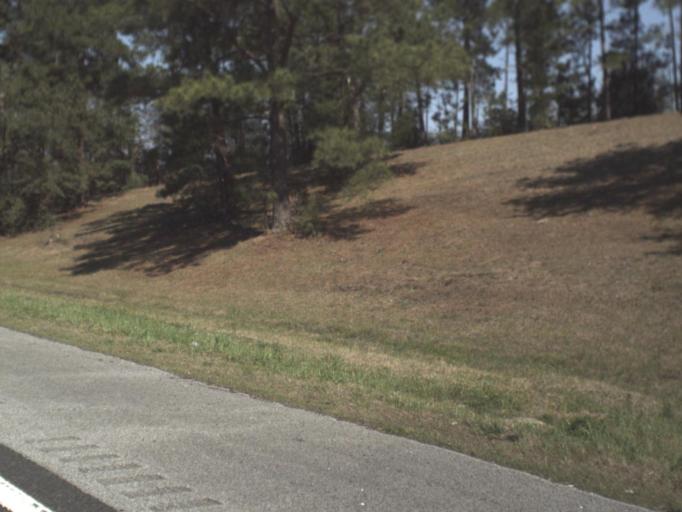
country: US
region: Florida
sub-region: Jackson County
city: Sneads
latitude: 30.6623
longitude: -85.0473
